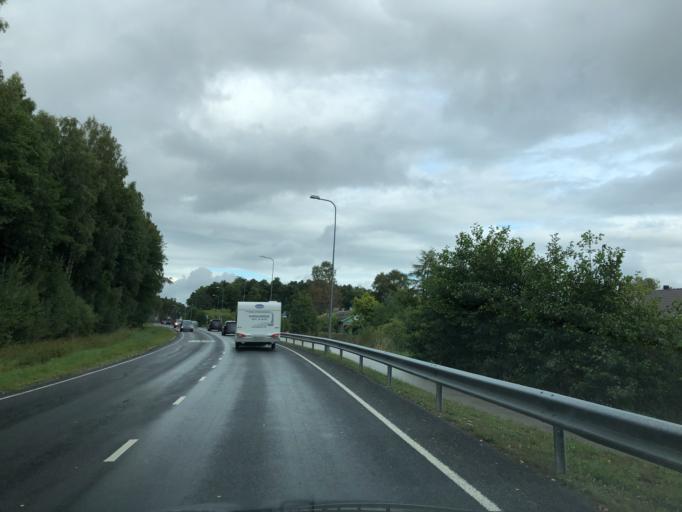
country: EE
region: Laeaene
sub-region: Haapsalu linn
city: Haapsalu
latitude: 58.9249
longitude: 23.5248
